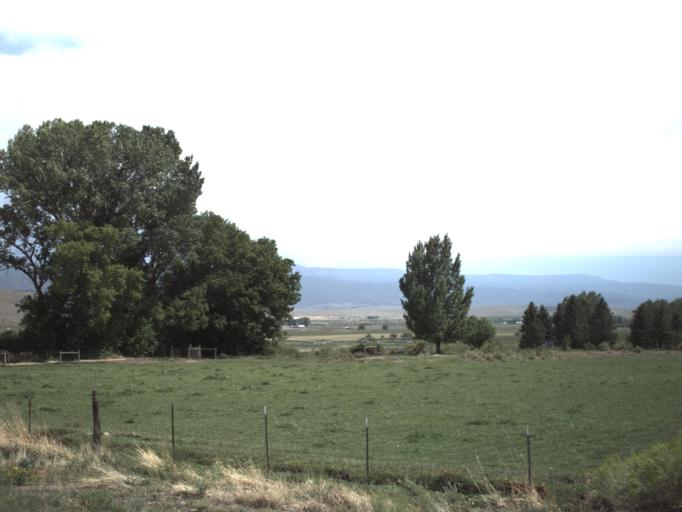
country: US
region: Utah
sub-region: Piute County
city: Junction
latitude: 38.1169
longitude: -112.0005
